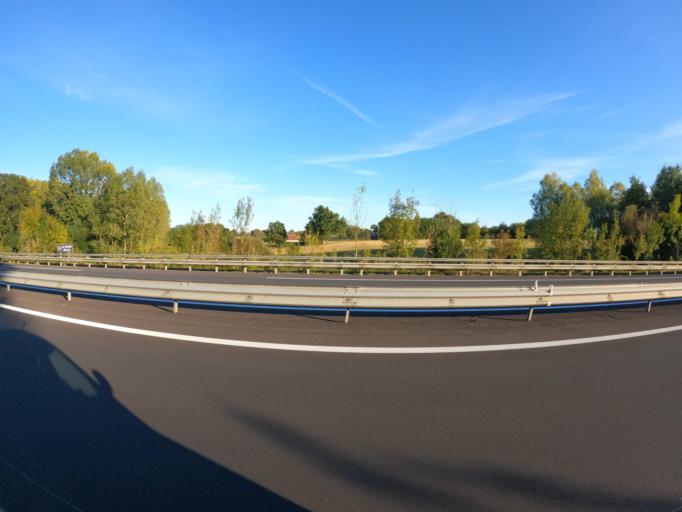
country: FR
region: Pays de la Loire
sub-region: Departement de la Vendee
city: Beaurepaire
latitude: 46.8810
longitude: -1.1078
